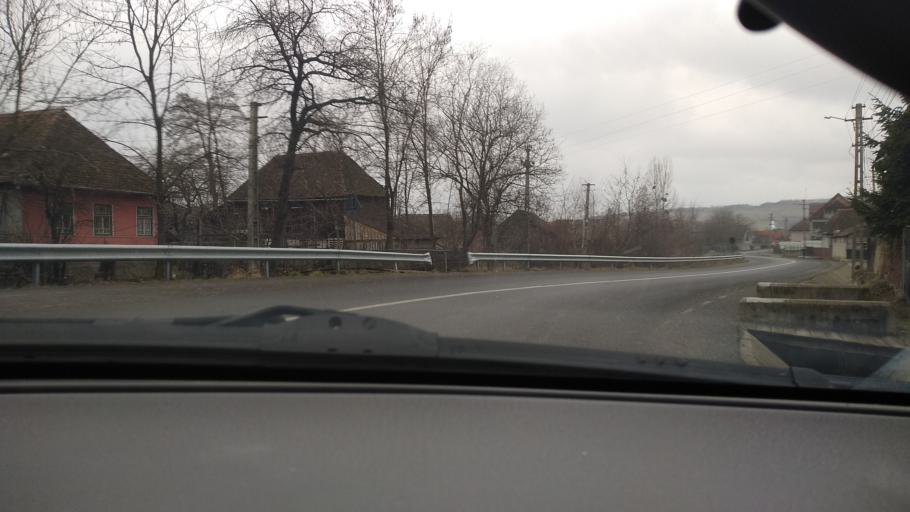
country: RO
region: Mures
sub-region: Comuna Magherani
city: Magherani
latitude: 46.5631
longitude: 24.9153
